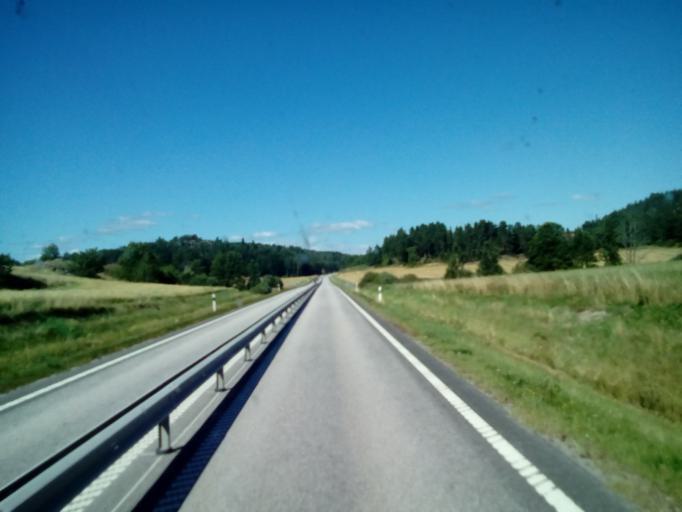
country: SE
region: OEstergoetland
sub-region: Kinda Kommun
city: Kisa
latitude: 58.0563
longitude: 15.6636
